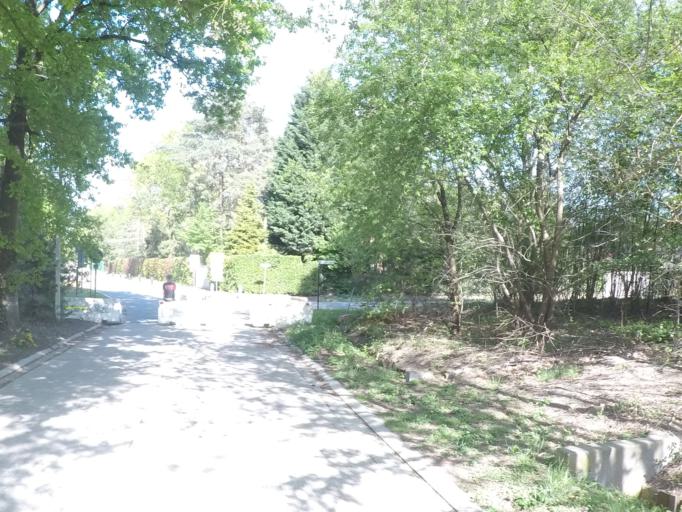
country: BE
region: Flanders
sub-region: Provincie Antwerpen
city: Grobbendonk
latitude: 51.1703
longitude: 4.7068
